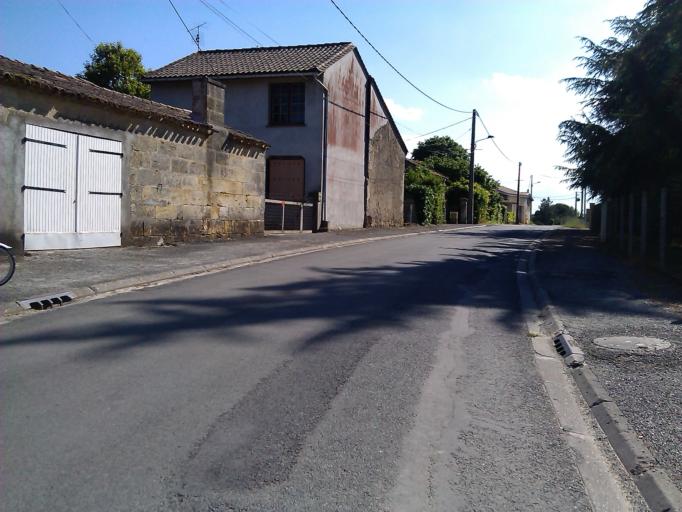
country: FR
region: Aquitaine
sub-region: Departement de la Gironde
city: Cezac
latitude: 45.0733
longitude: -0.4095
